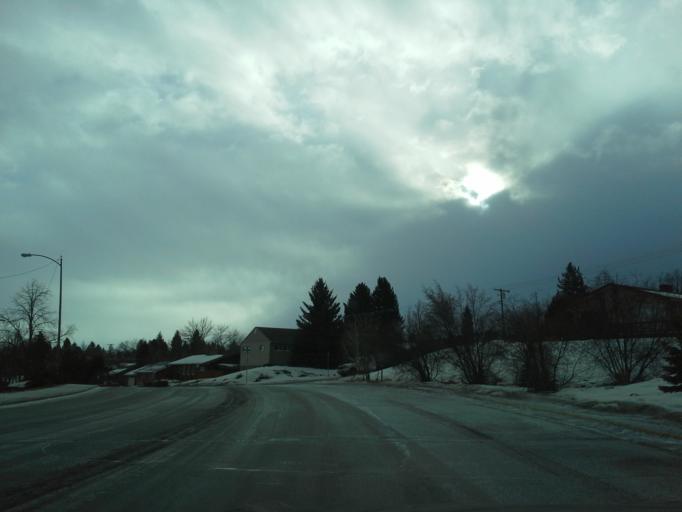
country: US
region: Montana
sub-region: Lewis and Clark County
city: Helena
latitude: 46.5842
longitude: -112.0192
